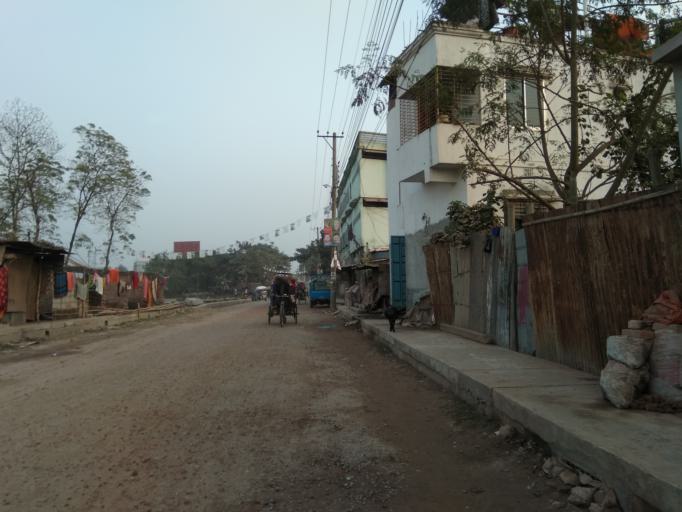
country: BD
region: Rangpur Division
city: Rangpur
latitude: 25.7328
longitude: 89.2624
